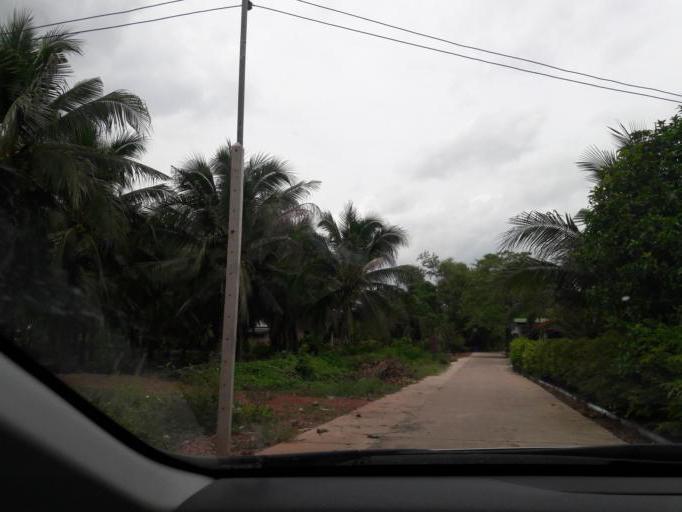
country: TH
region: Samut Sakhon
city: Ban Phaeo
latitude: 13.5921
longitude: 100.0295
